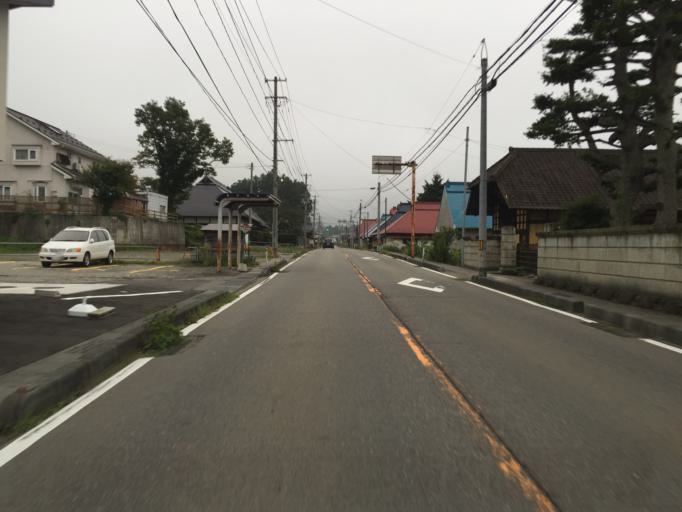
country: JP
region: Fukushima
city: Inawashiro
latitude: 37.3951
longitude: 139.9341
